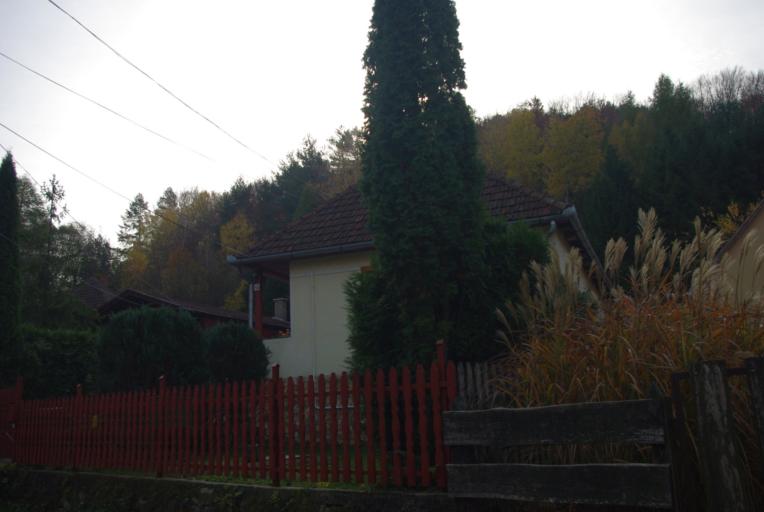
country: HU
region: Borsod-Abauj-Zemplen
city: Sarospatak
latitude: 48.4277
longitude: 21.4945
